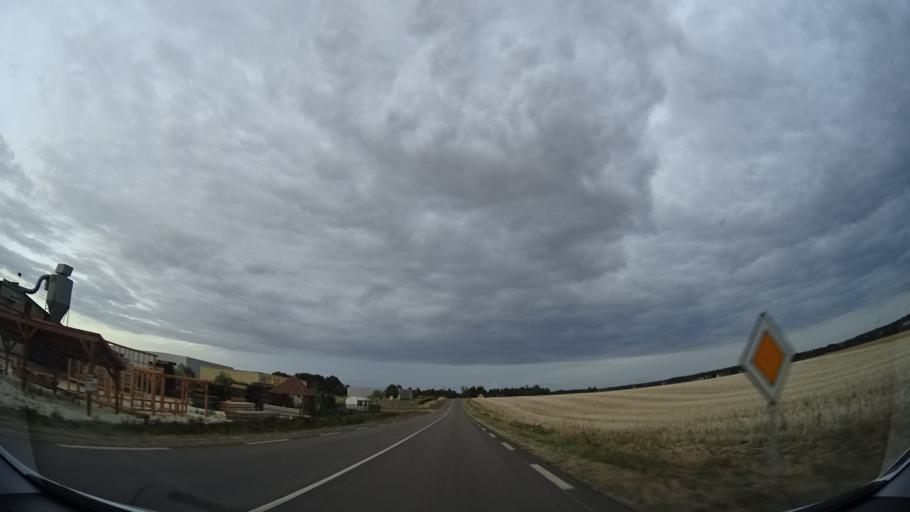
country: FR
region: Bourgogne
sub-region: Departement de l'Yonne
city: Charny
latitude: 47.9405
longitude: 3.1451
